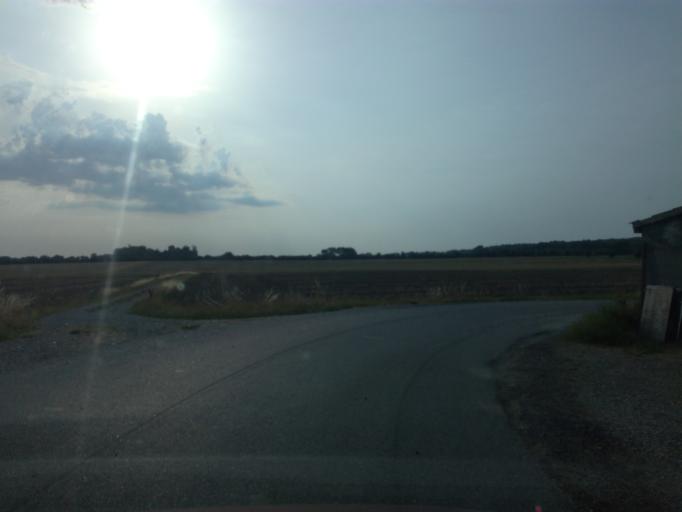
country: DK
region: South Denmark
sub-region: Vejle Kommune
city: Borkop
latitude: 55.6399
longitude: 9.6145
